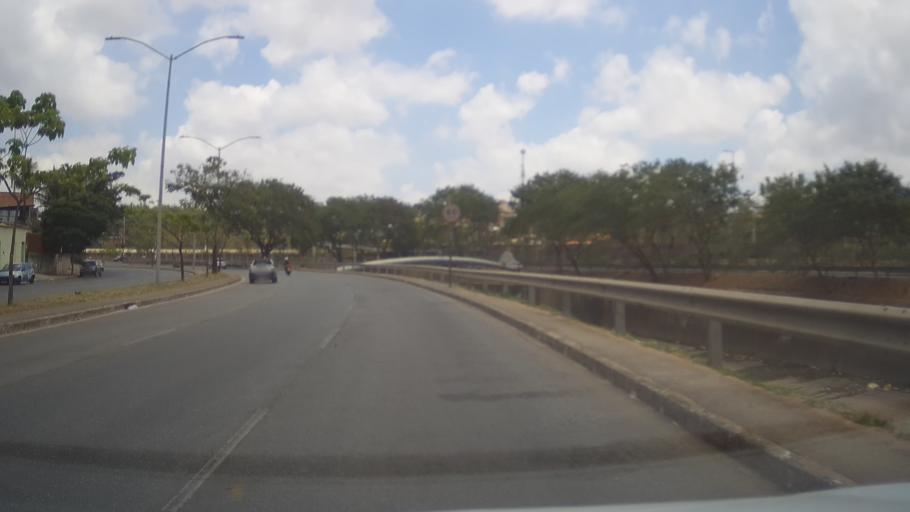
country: BR
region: Minas Gerais
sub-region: Belo Horizonte
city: Belo Horizonte
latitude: -19.9034
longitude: -43.8920
